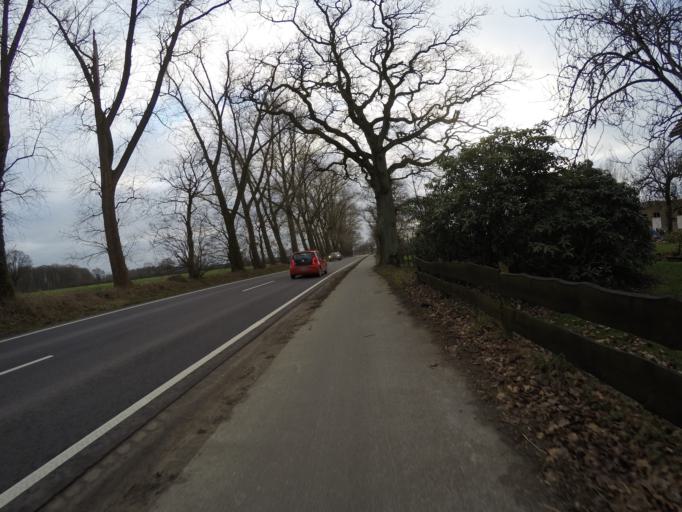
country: DE
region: Schleswig-Holstein
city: Alveslohe
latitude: 53.7775
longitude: 9.9078
